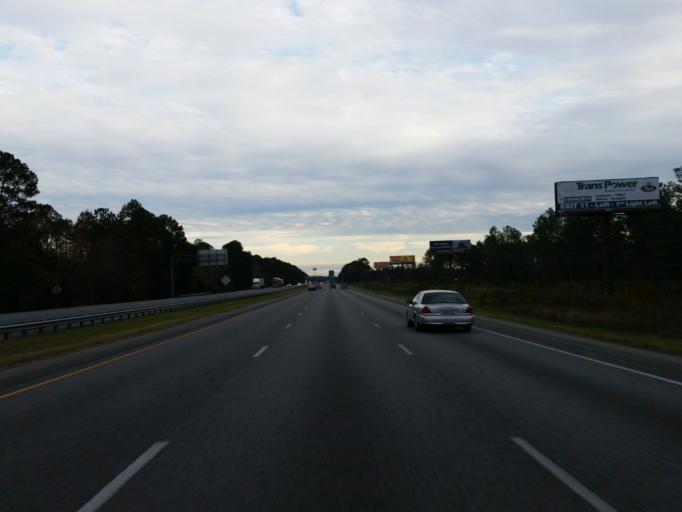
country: US
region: Georgia
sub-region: Lowndes County
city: Valdosta
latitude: 30.7691
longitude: -83.2896
